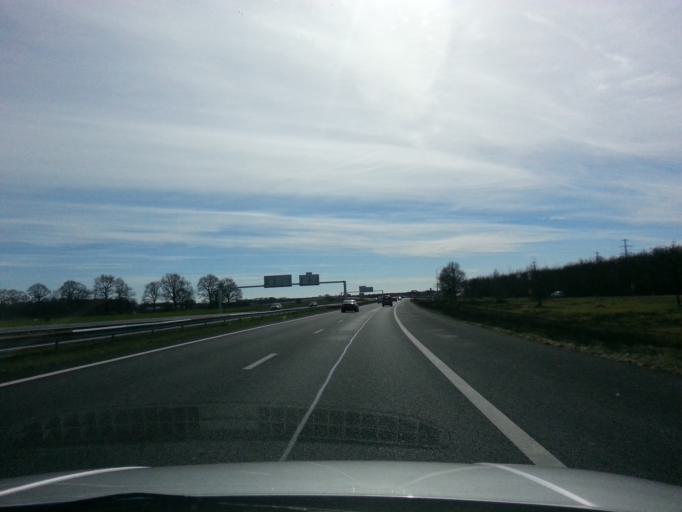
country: NL
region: Drenthe
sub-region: Gemeente Assen
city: Assen
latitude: 52.9637
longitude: 6.5466
